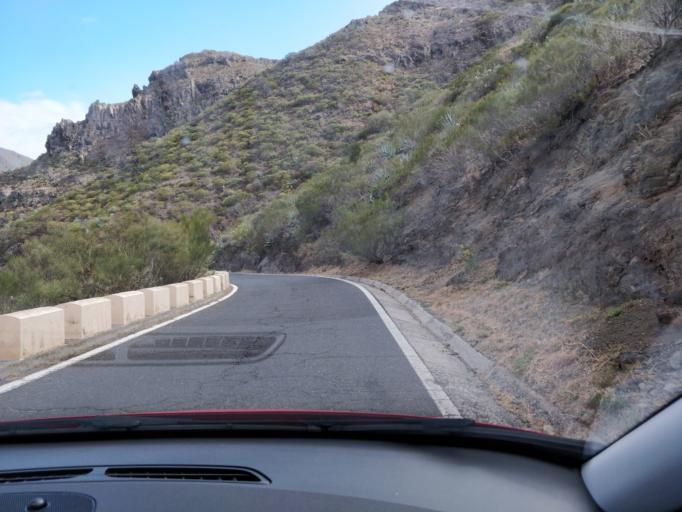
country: ES
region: Canary Islands
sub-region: Provincia de Santa Cruz de Tenerife
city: Santiago del Teide
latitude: 28.3117
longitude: -16.8468
